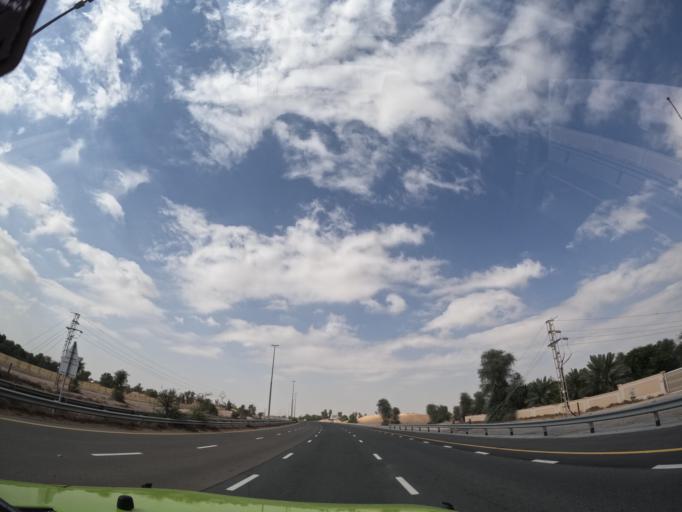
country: AE
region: Ash Shariqah
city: Sharjah
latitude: 25.0362
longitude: 55.5854
